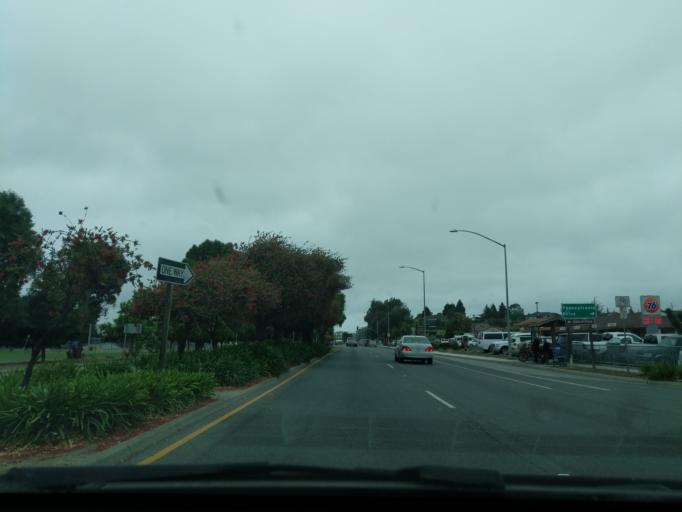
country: US
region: California
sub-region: Santa Cruz County
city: Watsonville
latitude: 36.9163
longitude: -121.7696
